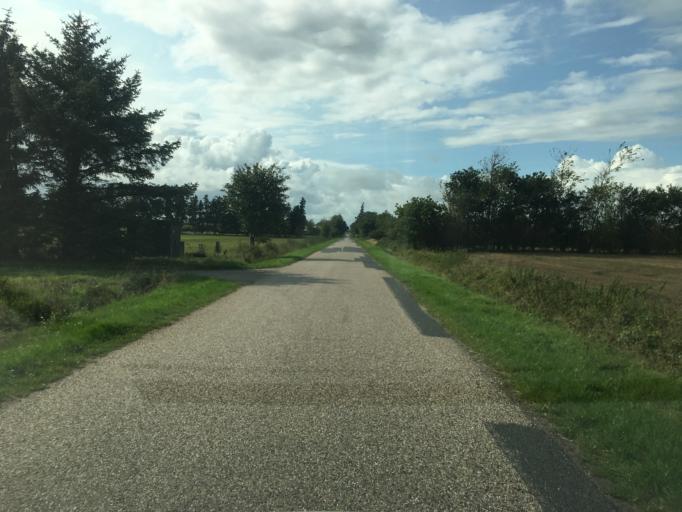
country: DK
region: South Denmark
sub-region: Tonder Kommune
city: Tonder
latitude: 54.9787
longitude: 8.8395
